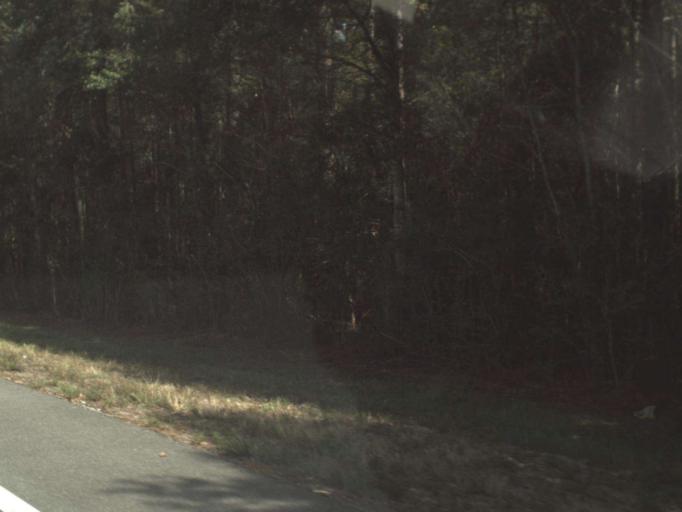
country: US
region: Florida
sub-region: Washington County
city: Chipley
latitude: 30.8215
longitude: -85.5331
